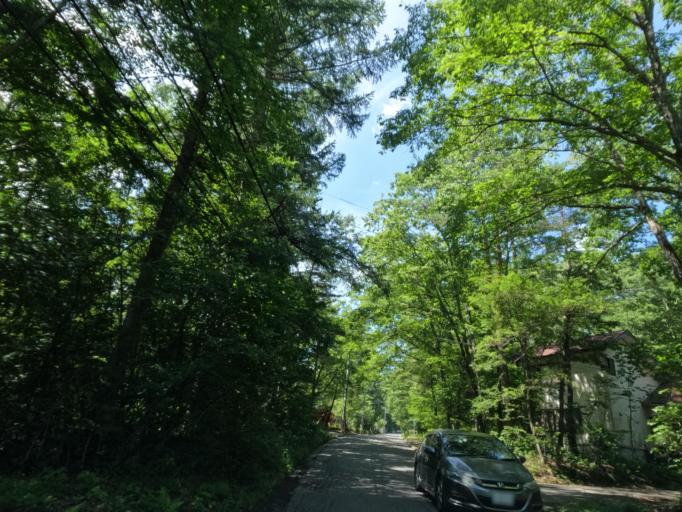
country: JP
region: Nagano
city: Komoro
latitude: 36.4670
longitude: 138.5617
